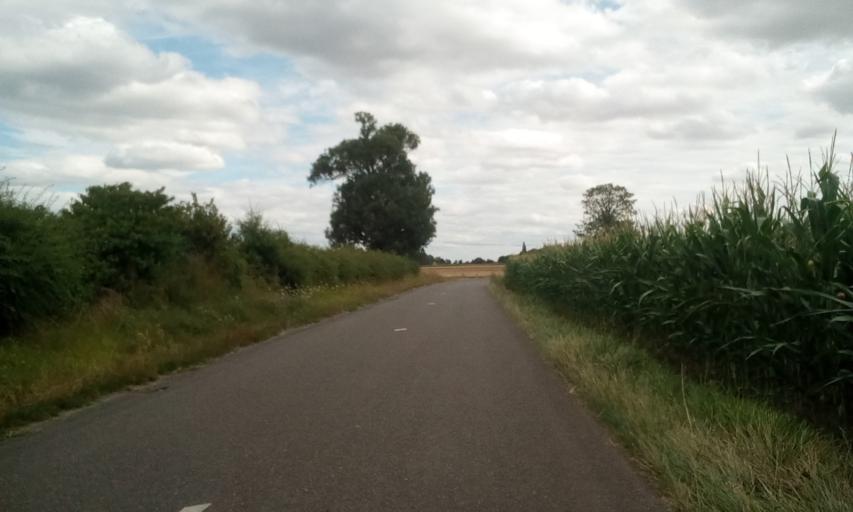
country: FR
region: Lower Normandy
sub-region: Departement du Calvados
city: Bellengreville
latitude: 49.1376
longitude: -0.2044
